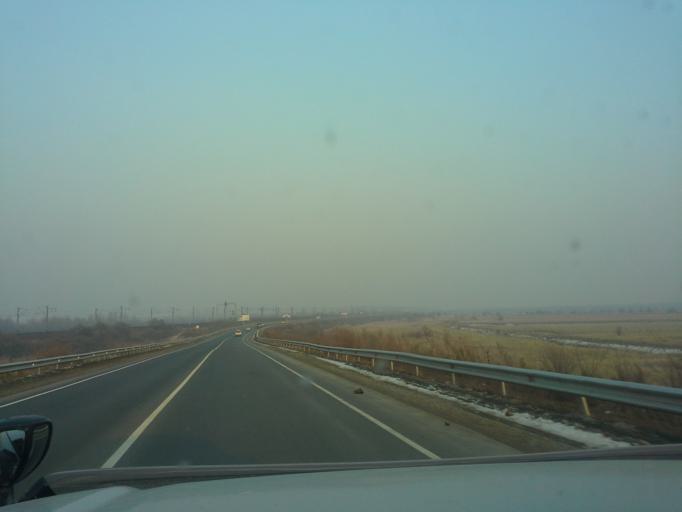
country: RU
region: Jewish Autonomous Oblast
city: Priamurskiy
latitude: 48.5235
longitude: 134.9201
